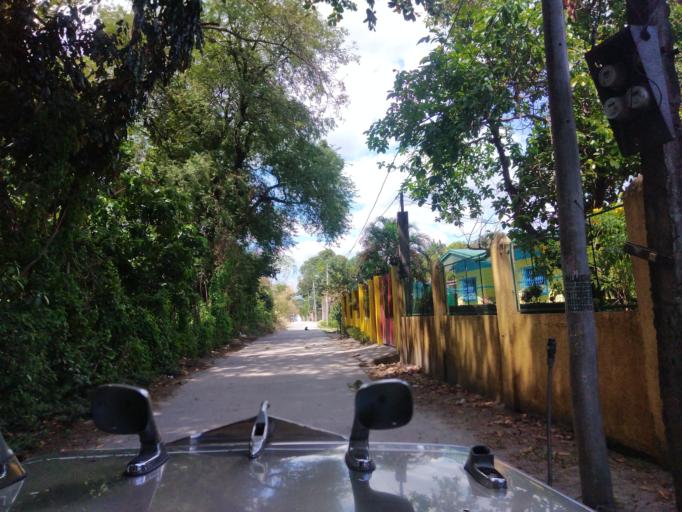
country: PH
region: Central Luzon
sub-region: Province of Pampanga
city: San Basilio
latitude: 15.0156
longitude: 120.5878
